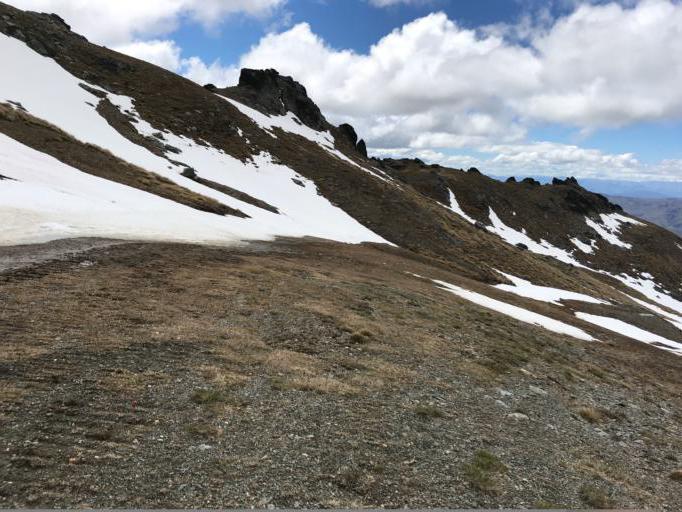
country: NZ
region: Otago
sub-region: Queenstown-Lakes District
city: Arrowtown
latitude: -44.8576
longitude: 168.9462
